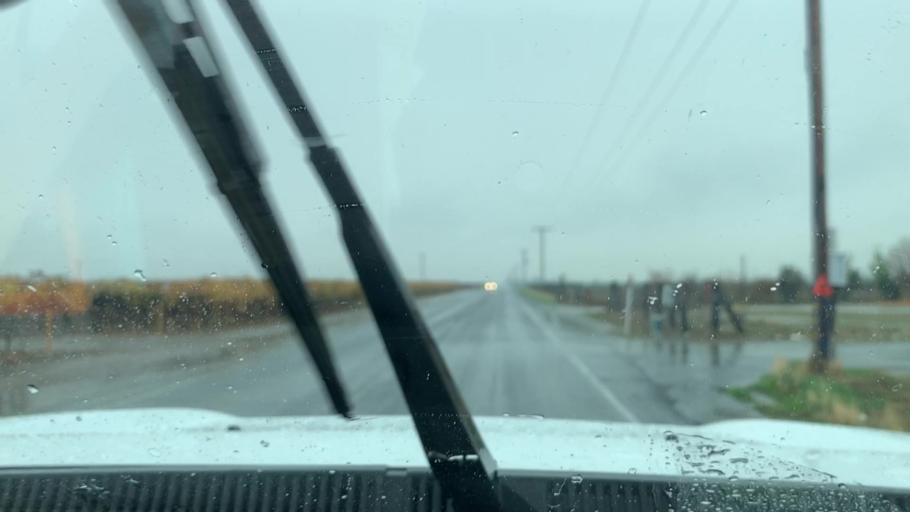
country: US
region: California
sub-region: Tulare County
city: Earlimart
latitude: 35.8919
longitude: -119.2925
